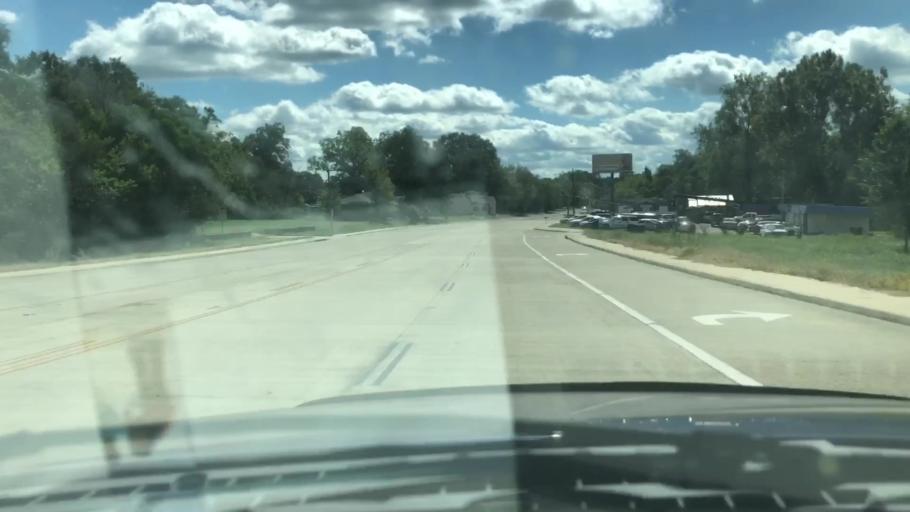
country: US
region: Texas
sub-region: Bowie County
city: Texarkana
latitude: 33.4117
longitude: -94.0608
